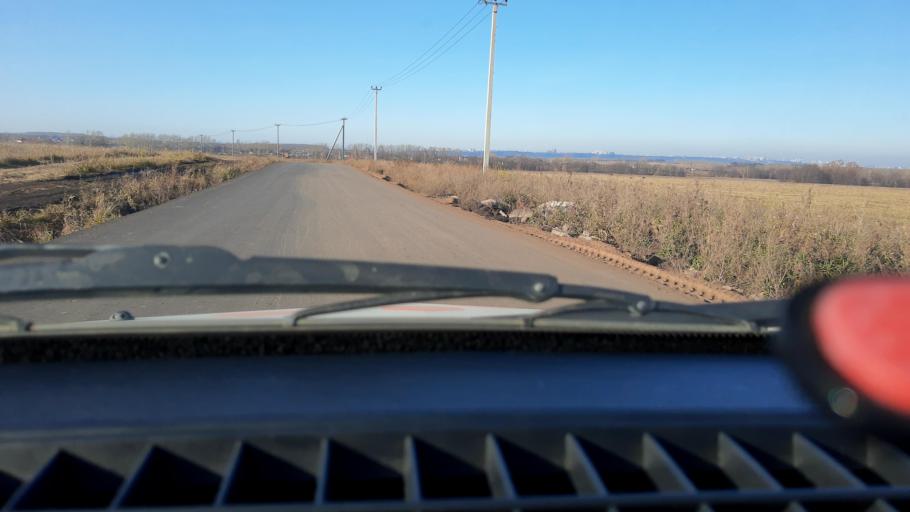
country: RU
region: Bashkortostan
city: Kabakovo
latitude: 54.6223
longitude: 56.1534
